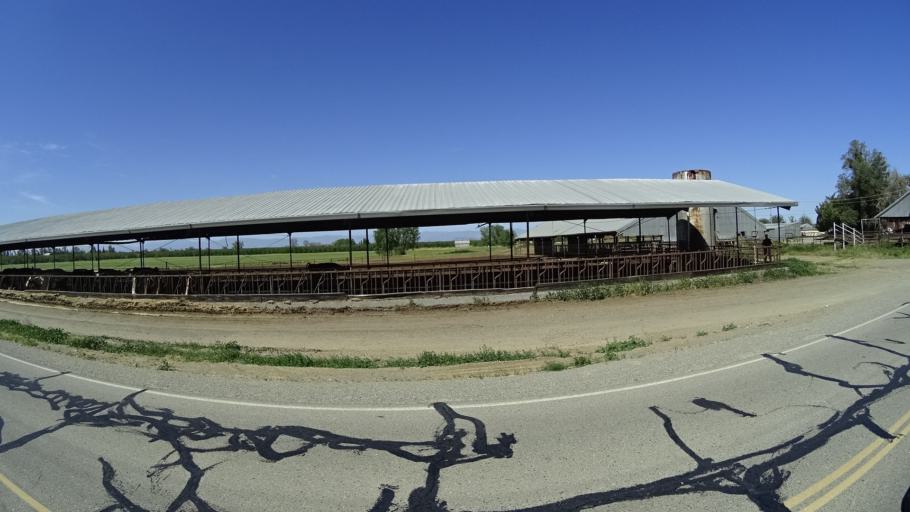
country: US
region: California
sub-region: Glenn County
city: Hamilton City
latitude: 39.7383
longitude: -122.1042
